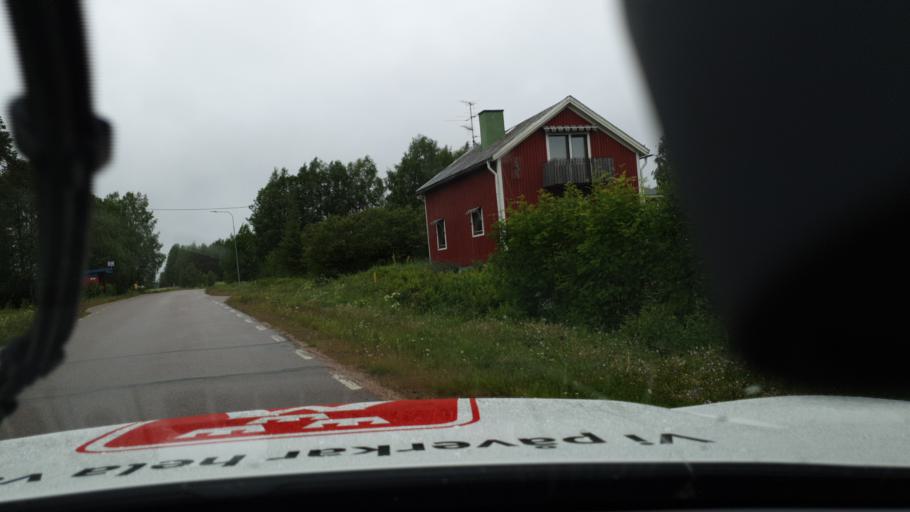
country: SE
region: Norrbotten
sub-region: Overtornea Kommun
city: OEvertornea
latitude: 66.5657
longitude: 23.4246
